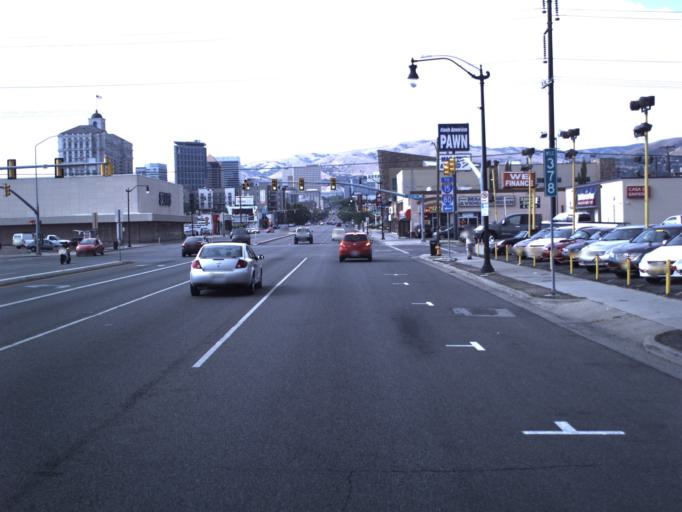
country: US
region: Utah
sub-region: Salt Lake County
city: Salt Lake City
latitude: 40.7513
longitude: -111.8881
